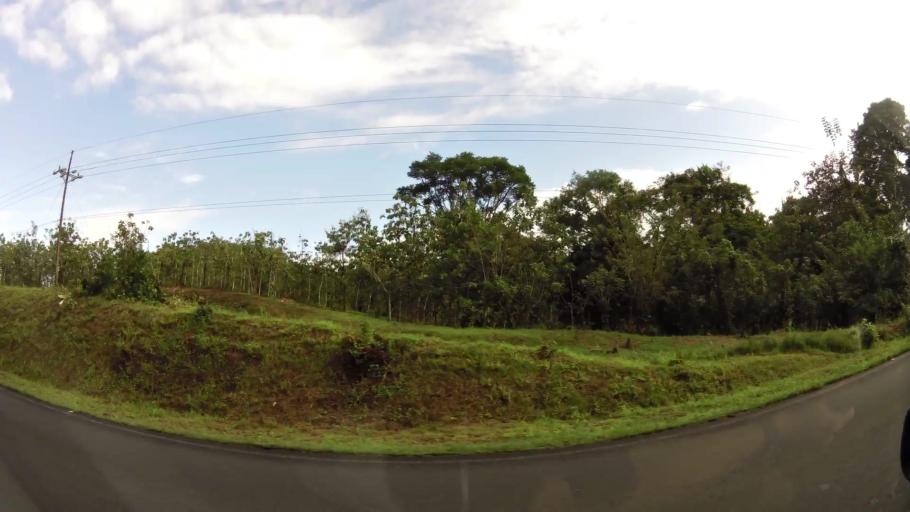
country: CR
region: Limon
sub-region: Canton de Guacimo
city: Guacimo
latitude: 10.1970
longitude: -83.6535
